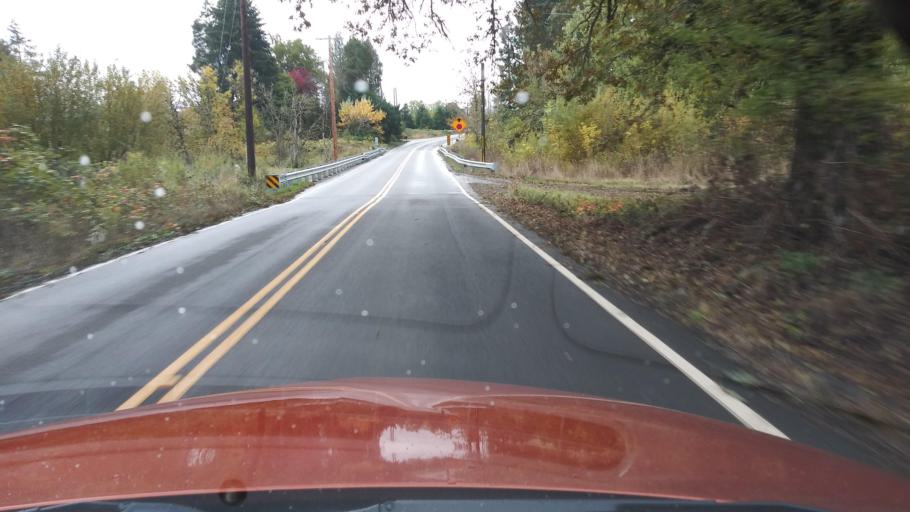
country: US
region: Oregon
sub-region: Washington County
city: Forest Grove
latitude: 45.5306
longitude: -123.0871
